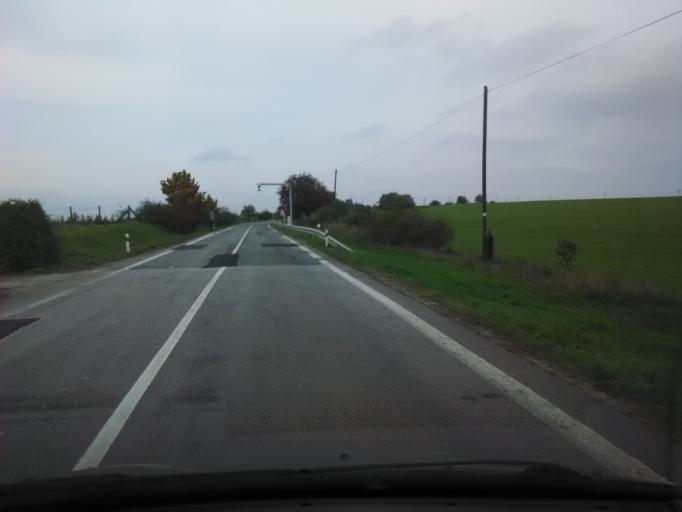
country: SK
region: Nitriansky
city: Svodin
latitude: 48.0221
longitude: 18.4212
